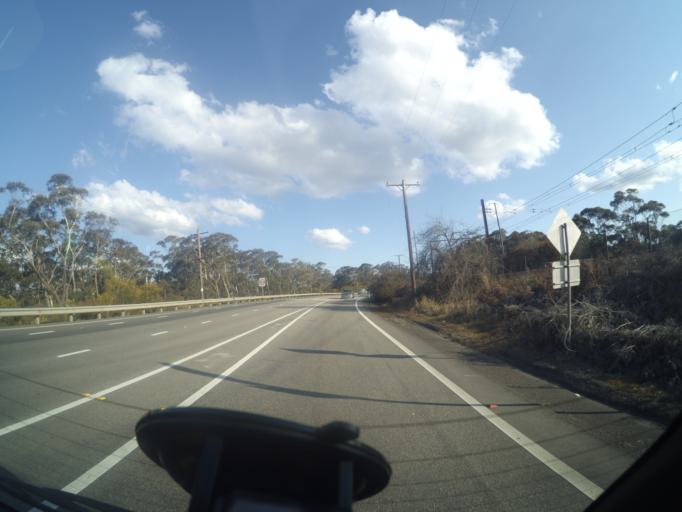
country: AU
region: New South Wales
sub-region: Blue Mountains Municipality
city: Blackheath
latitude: -33.6509
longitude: 150.2849
